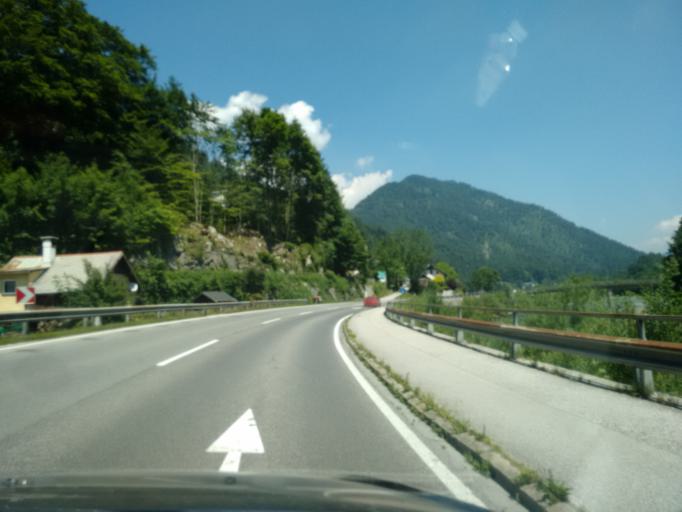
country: AT
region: Upper Austria
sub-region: Politischer Bezirk Gmunden
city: Bad Ischl
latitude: 47.7372
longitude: 13.6587
